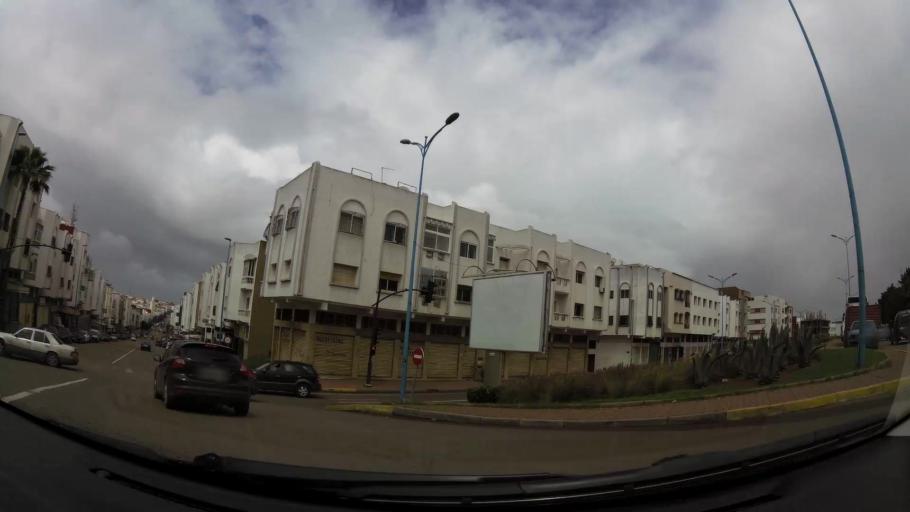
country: MA
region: Grand Casablanca
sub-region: Casablanca
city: Casablanca
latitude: 33.5400
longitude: -7.6761
